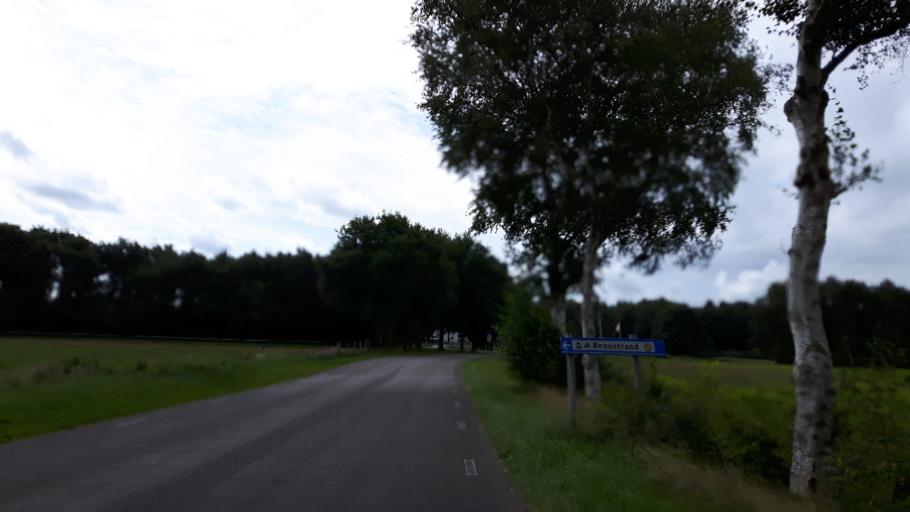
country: NL
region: Groningen
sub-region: Gemeente Leek
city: Leek
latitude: 53.1030
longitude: 6.3740
